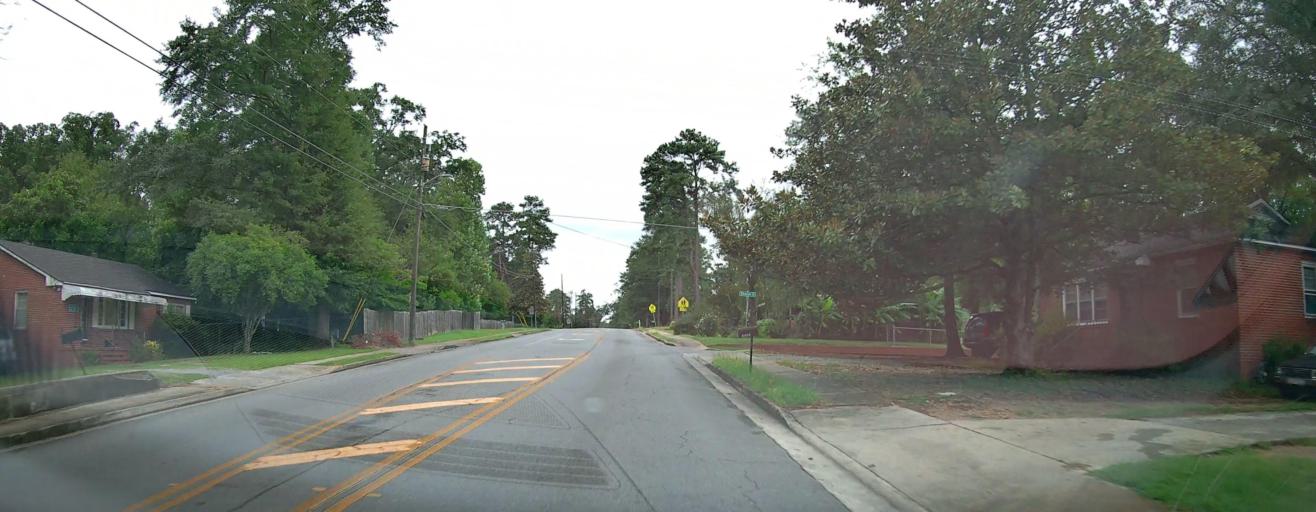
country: US
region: Georgia
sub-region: Bibb County
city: Macon
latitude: 32.8330
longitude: -83.6869
